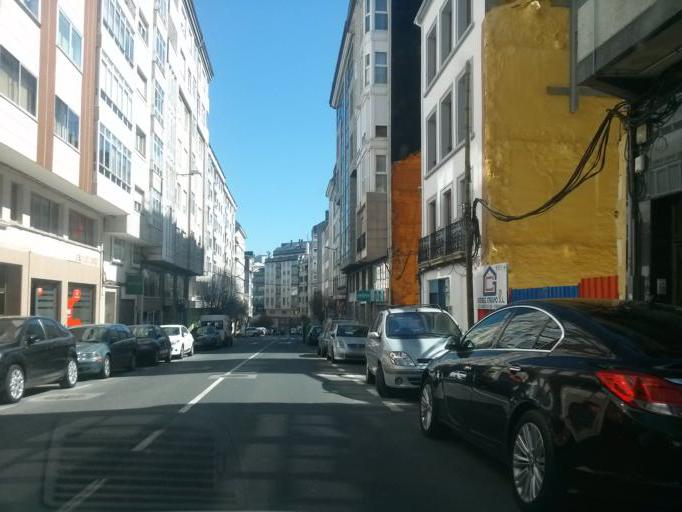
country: ES
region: Galicia
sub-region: Provincia de Lugo
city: Lugo
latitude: 43.0144
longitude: -7.5542
